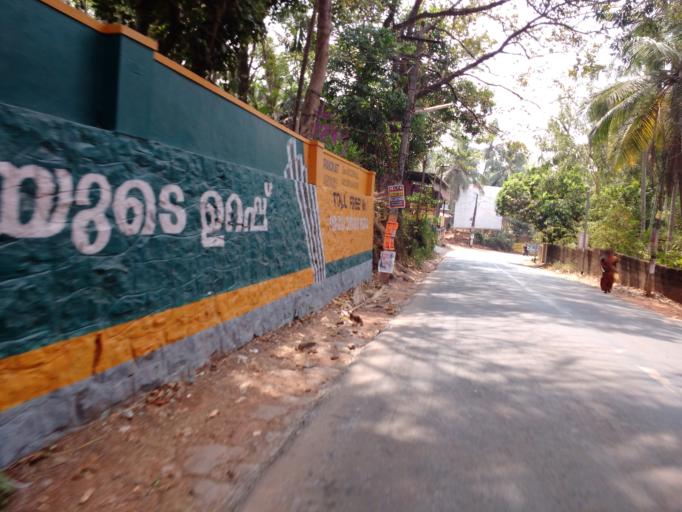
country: IN
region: Kerala
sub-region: Kozhikode
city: Kunnamangalam
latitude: 11.3000
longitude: 75.8619
